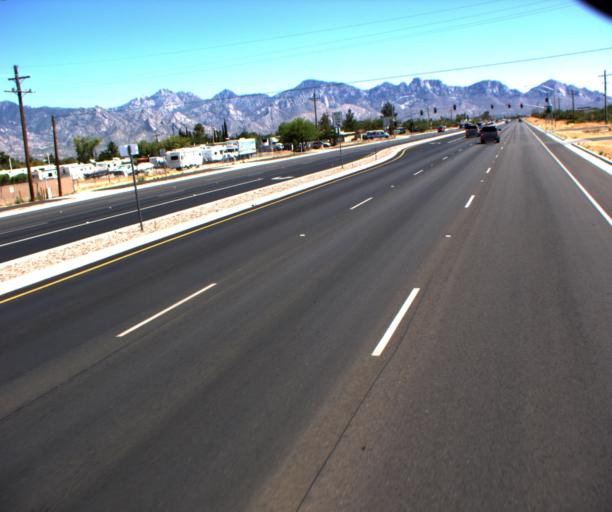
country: US
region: Arizona
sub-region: Pima County
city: Catalina
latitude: 32.5089
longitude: -110.9259
